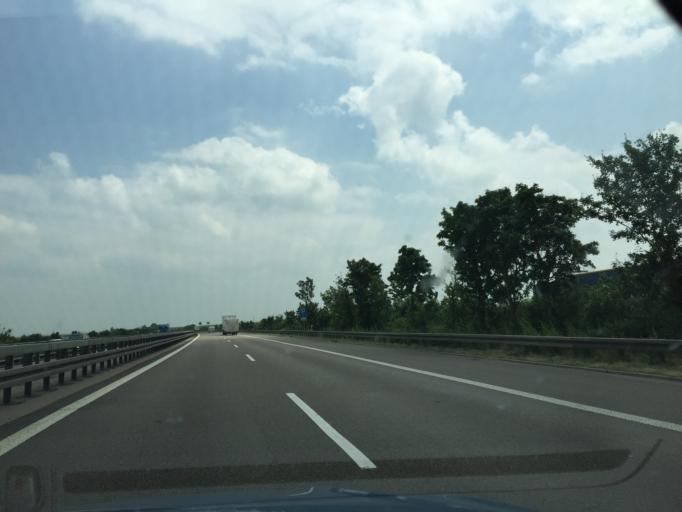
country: DE
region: Baden-Wuerttemberg
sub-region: Tuebingen Region
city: Langenau
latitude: 48.4929
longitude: 10.0885
